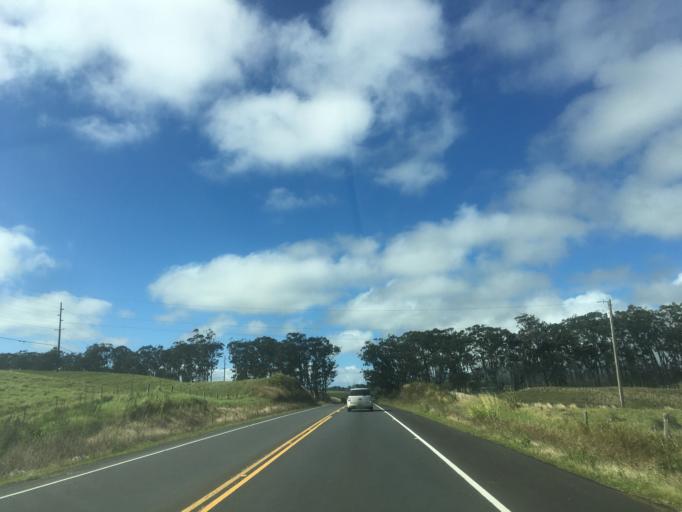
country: US
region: Hawaii
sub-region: Hawaii County
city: Waimea
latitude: 20.0498
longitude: -155.5699
